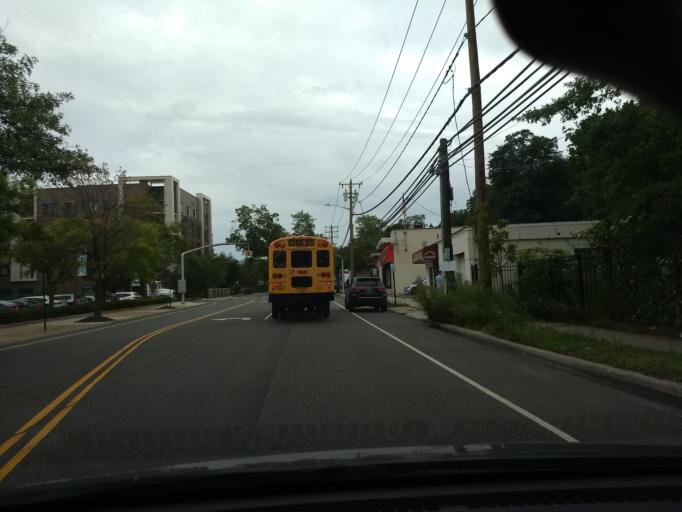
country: US
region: New York
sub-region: Nassau County
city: Kensington
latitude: 40.7975
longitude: -73.7134
